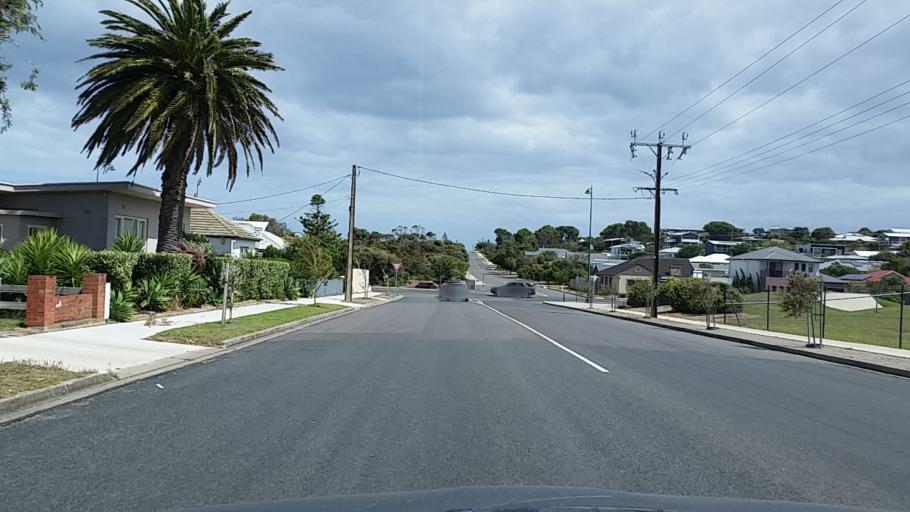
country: AU
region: South Australia
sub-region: Alexandrina
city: Port Elliot
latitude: -35.5301
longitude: 138.6768
